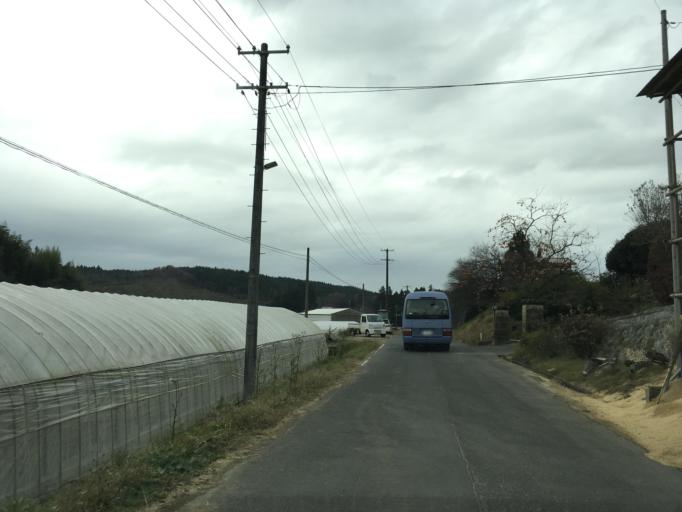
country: JP
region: Iwate
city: Ichinoseki
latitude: 38.8443
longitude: 141.0334
